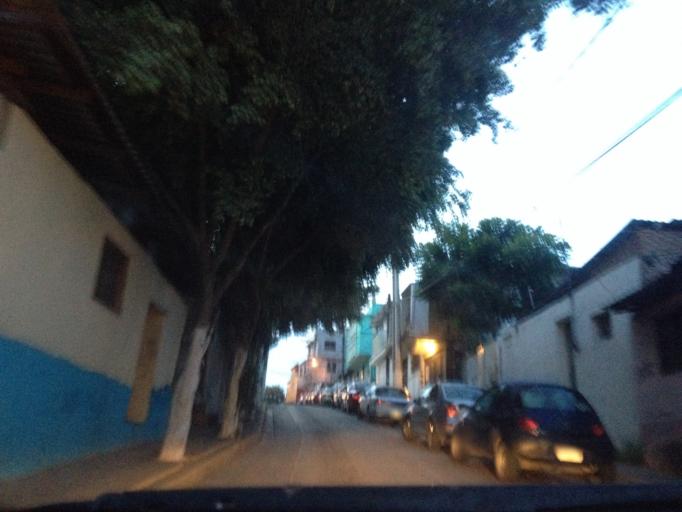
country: MX
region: Guerrero
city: Chilpancingo de los Bravos
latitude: 17.5584
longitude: -99.5017
